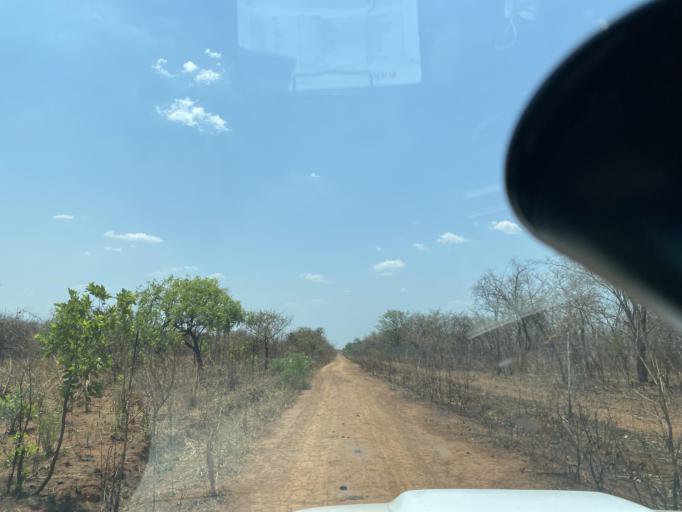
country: ZM
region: Lusaka
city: Lusaka
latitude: -15.5039
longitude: 27.9702
